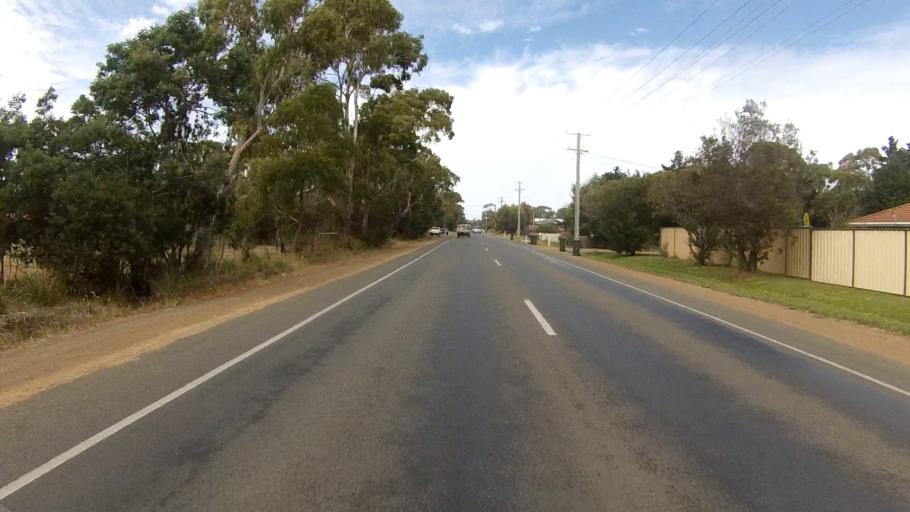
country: AU
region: Tasmania
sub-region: Clarence
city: Sandford
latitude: -42.9370
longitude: 147.4939
